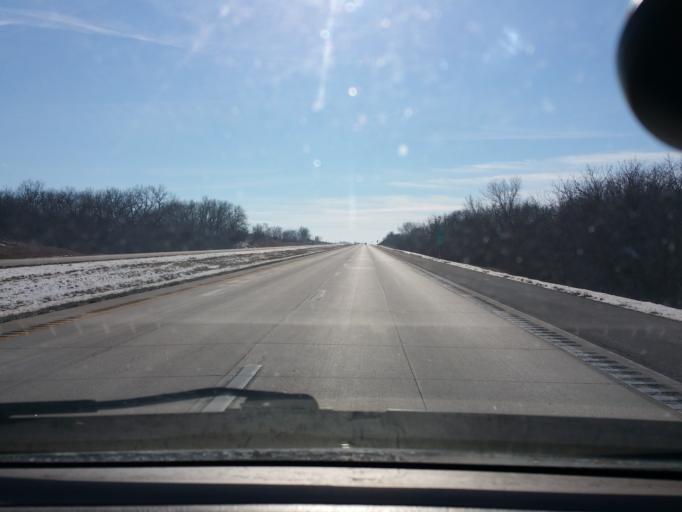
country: US
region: Missouri
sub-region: Daviess County
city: Gallatin
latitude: 39.9839
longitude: -94.0950
